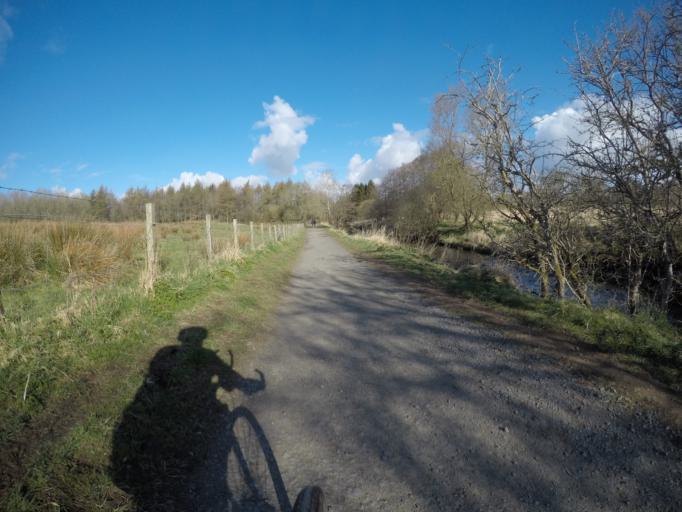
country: GB
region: Scotland
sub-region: North Ayrshire
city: Irvine
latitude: 55.6432
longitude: -4.6637
